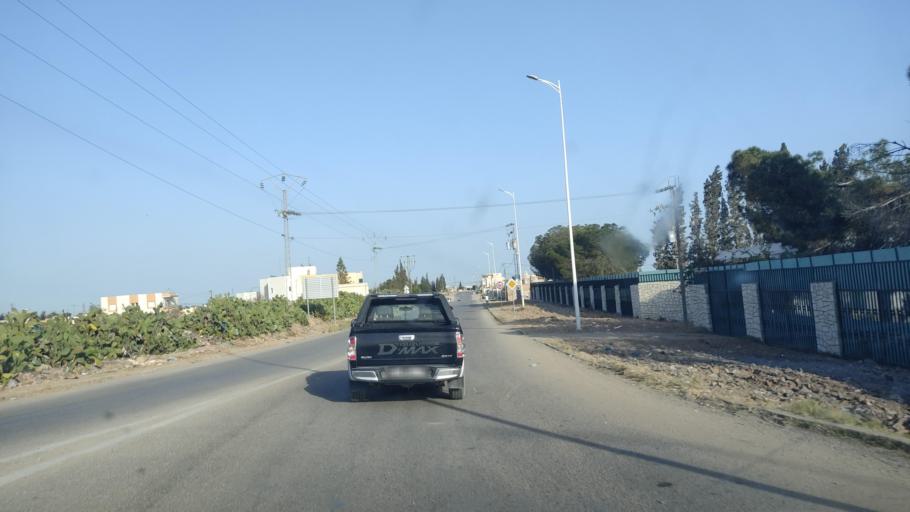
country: TN
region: Safaqis
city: Sfax
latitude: 34.7966
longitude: 10.6794
